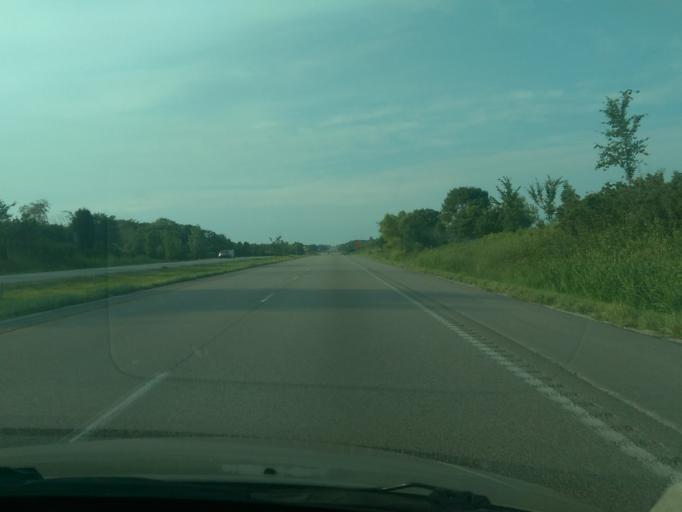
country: US
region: Missouri
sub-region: Platte County
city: Platte City
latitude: 39.4414
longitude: -94.7891
